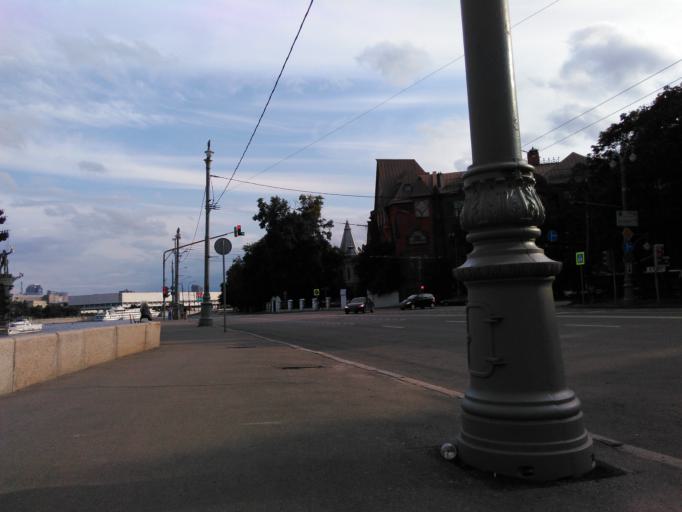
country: RU
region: Moscow
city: Moscow
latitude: 55.7431
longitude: 37.6074
